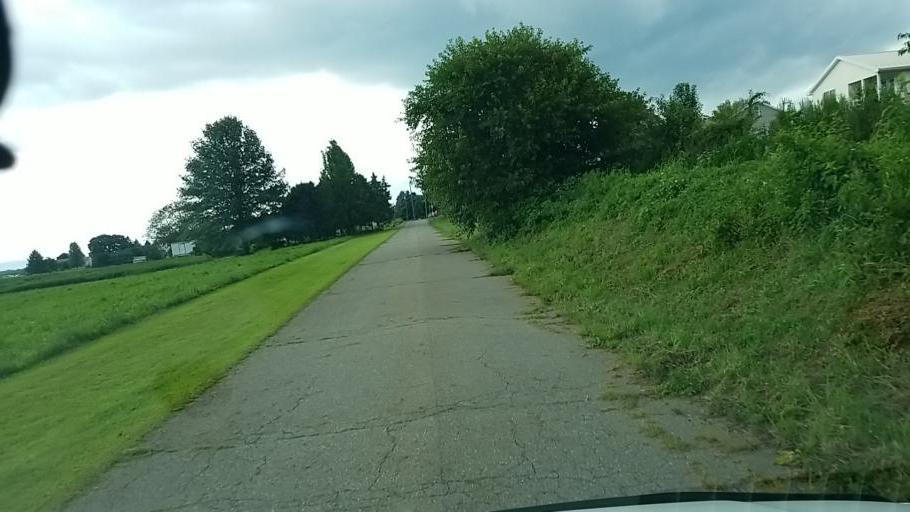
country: US
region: Pennsylvania
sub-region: Dauphin County
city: Elizabethville
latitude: 40.6014
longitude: -76.8067
